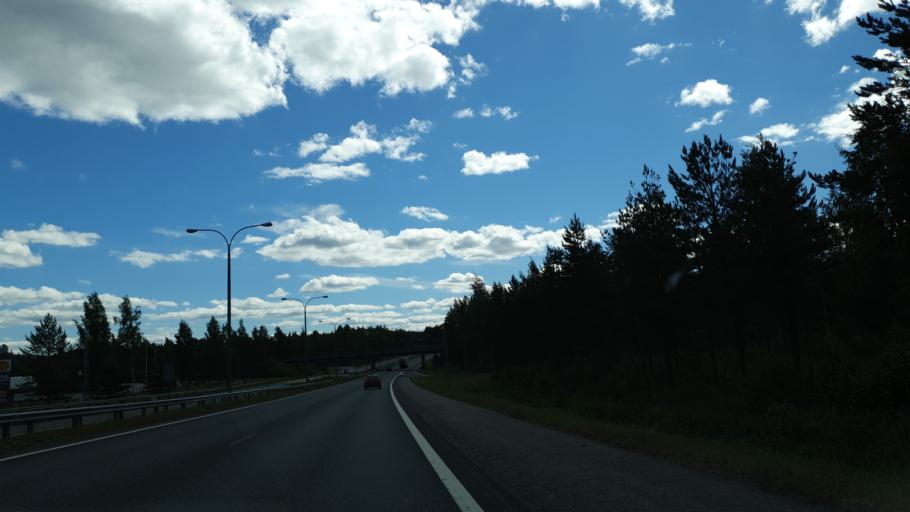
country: FI
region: Northern Savo
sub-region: Kuopio
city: Siilinjaervi
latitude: 63.0611
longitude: 27.6707
